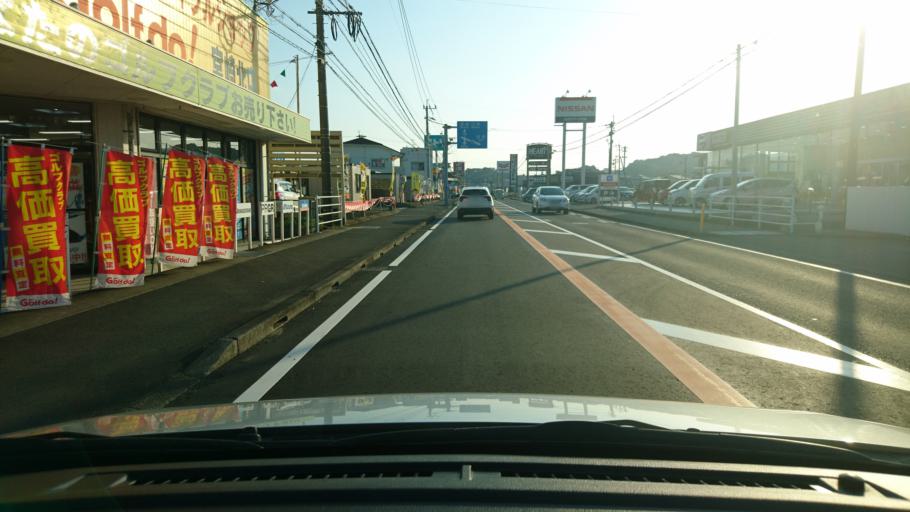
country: JP
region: Miyazaki
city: Miyazaki-shi
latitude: 31.9786
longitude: 131.4447
